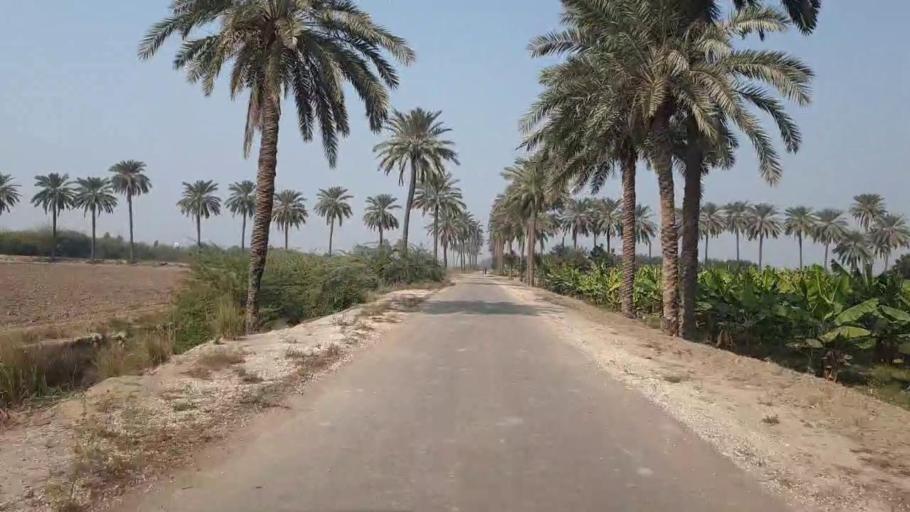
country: PK
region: Sindh
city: Bhit Shah
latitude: 25.7778
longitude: 68.4779
